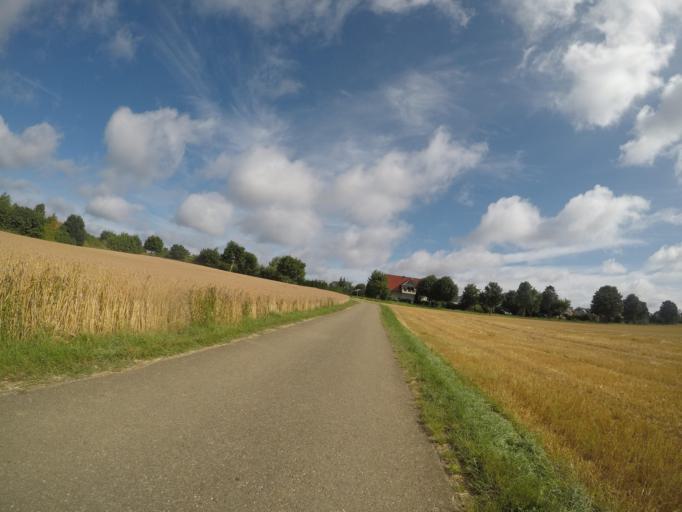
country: DE
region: Baden-Wuerttemberg
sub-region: Tuebingen Region
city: Laichingen
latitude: 48.4378
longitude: 9.6587
